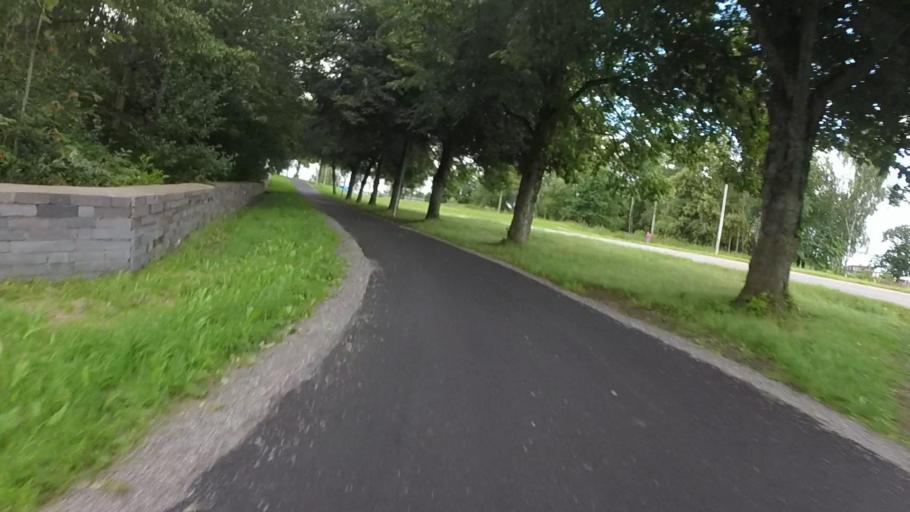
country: SE
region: Vaestra Goetaland
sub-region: Trollhattan
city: Trollhattan
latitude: 58.2764
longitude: 12.3108
